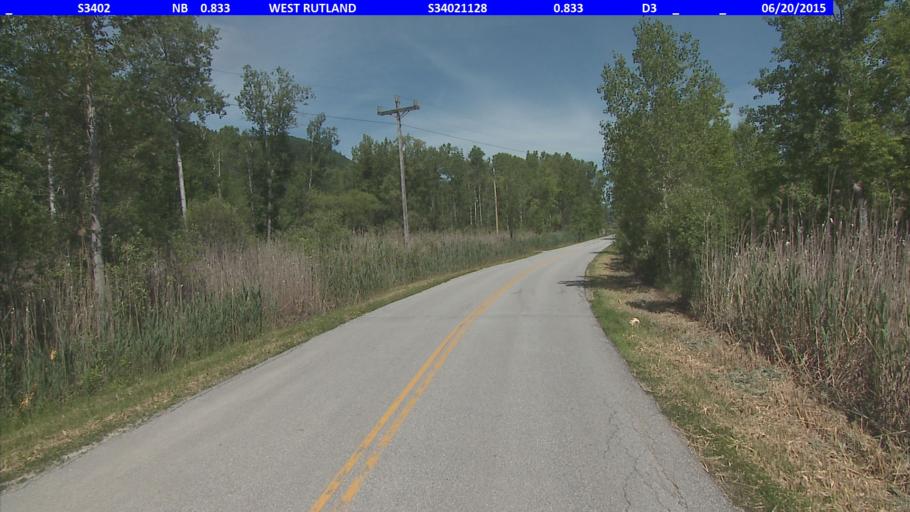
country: US
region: Vermont
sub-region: Rutland County
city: West Rutland
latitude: 43.6055
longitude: -73.0544
